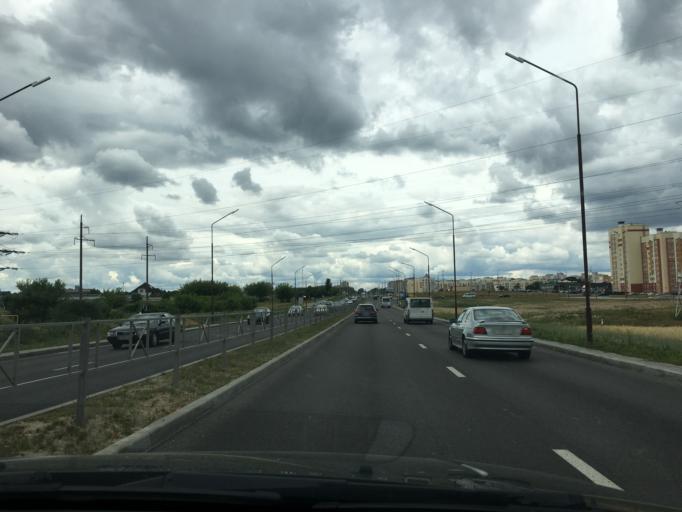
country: BY
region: Grodnenskaya
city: Hrodna
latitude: 53.6326
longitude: 23.8534
